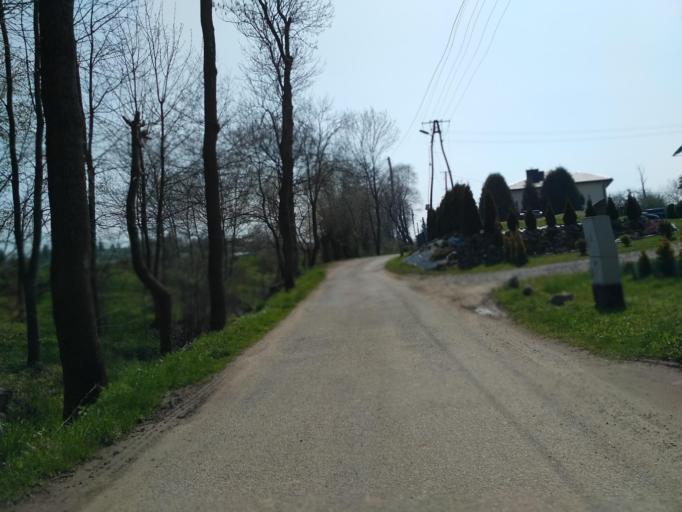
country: PL
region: Subcarpathian Voivodeship
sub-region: Powiat sanocki
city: Zarszyn
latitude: 49.6165
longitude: 22.0116
